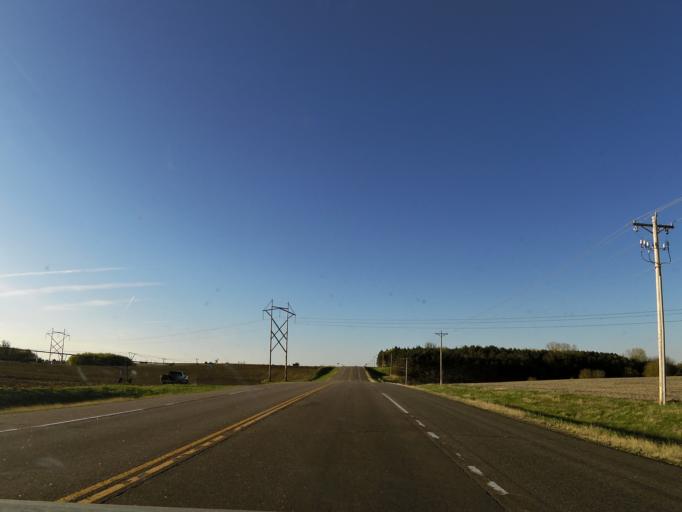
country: US
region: Wisconsin
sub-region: Pierce County
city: Prescott
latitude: 44.6258
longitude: -92.7724
